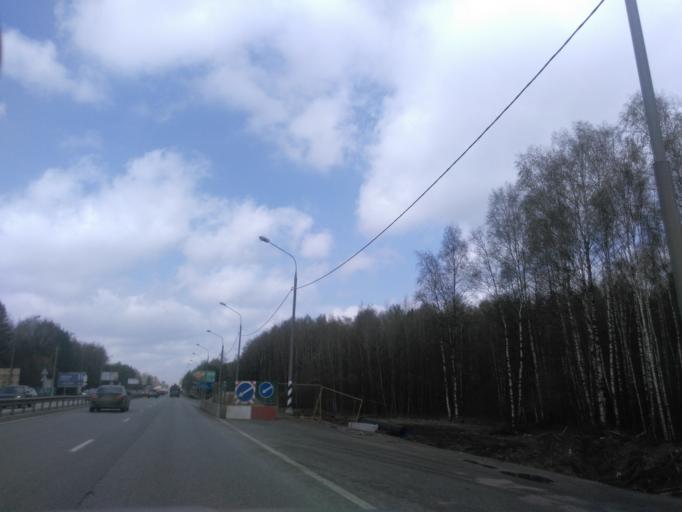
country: RU
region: Moskovskaya
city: Mendeleyevo
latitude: 56.0157
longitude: 37.2043
